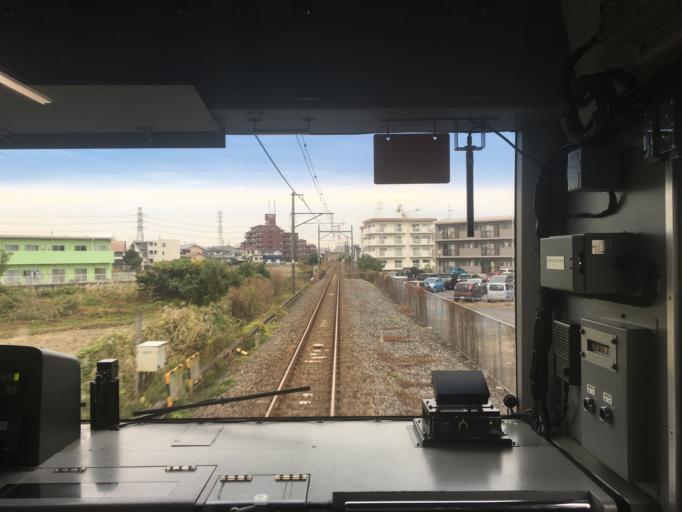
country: JP
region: Saitama
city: Kawagoe
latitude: 35.9151
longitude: 139.4733
